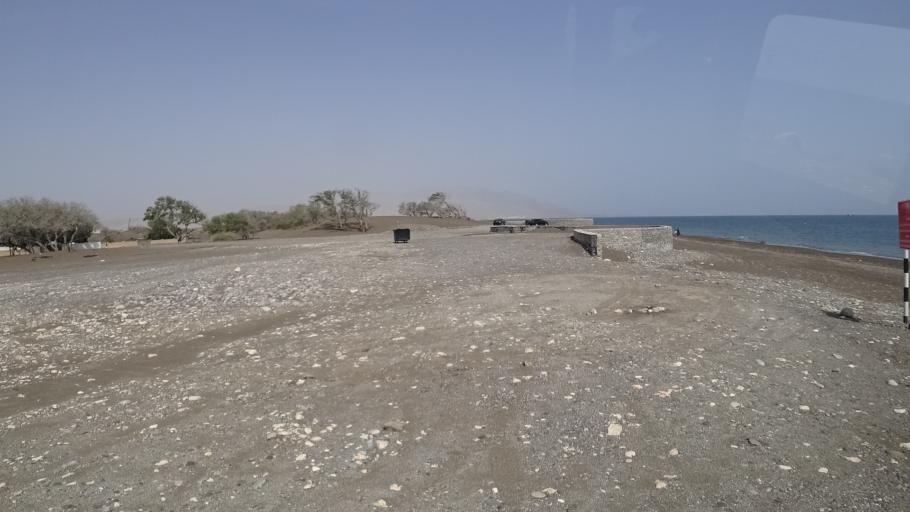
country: OM
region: Muhafazat Masqat
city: Muscat
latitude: 23.2181
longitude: 58.9754
